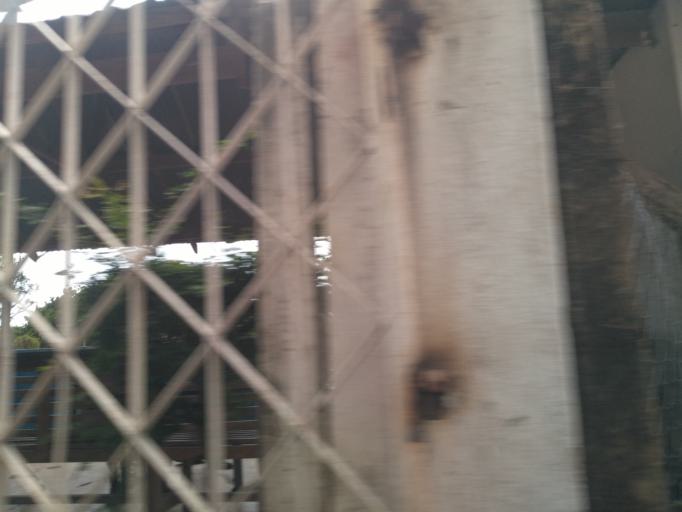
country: TZ
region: Dar es Salaam
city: Dar es Salaam
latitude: -6.8092
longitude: 39.2907
